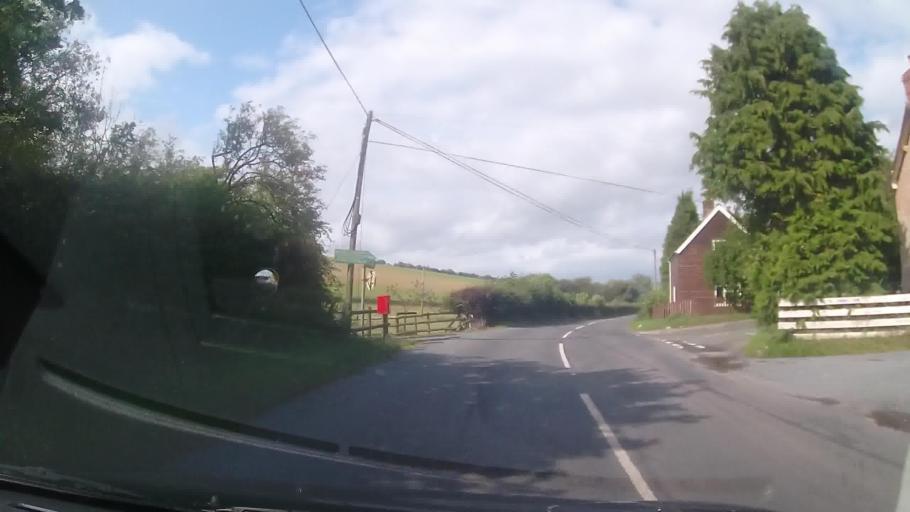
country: GB
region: Wales
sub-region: Sir Powys
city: Knighton
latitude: 52.3715
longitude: -3.0505
